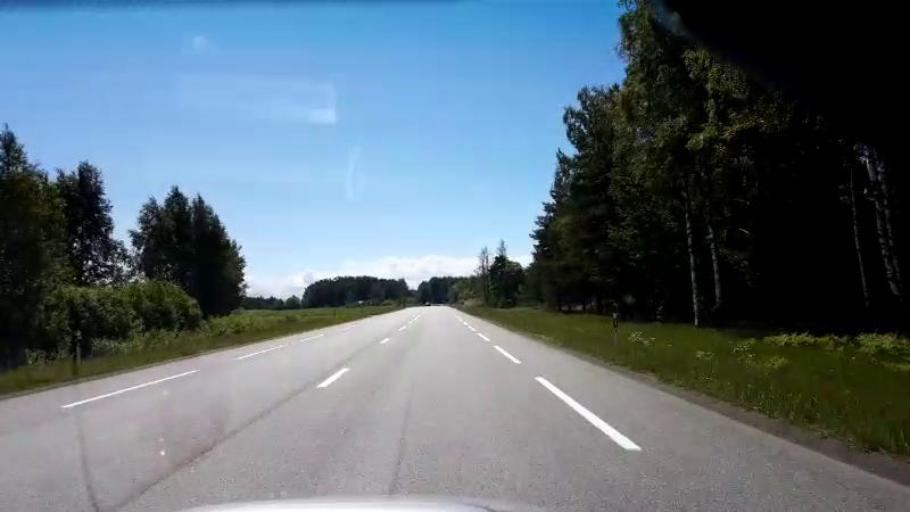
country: LV
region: Saulkrastu
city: Saulkrasti
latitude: 57.4422
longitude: 24.4294
